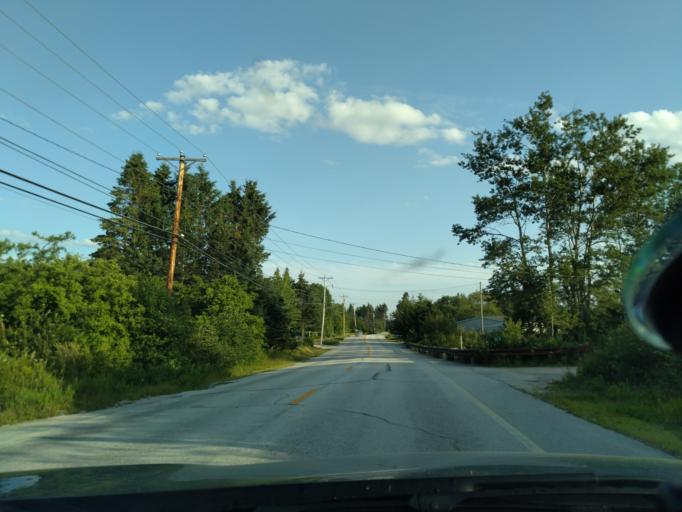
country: US
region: Maine
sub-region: Hancock County
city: Gouldsboro
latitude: 44.3996
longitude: -68.0857
